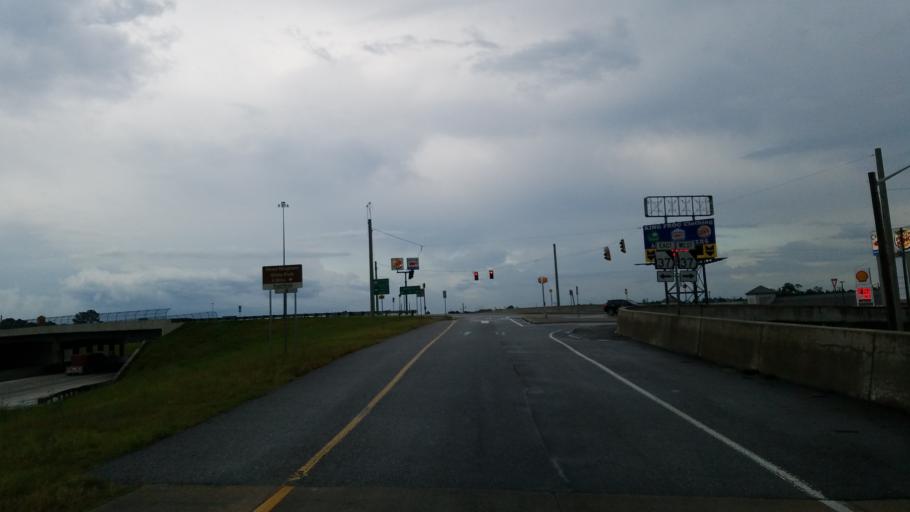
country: US
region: Georgia
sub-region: Cook County
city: Adel
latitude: 31.1373
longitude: -83.4399
